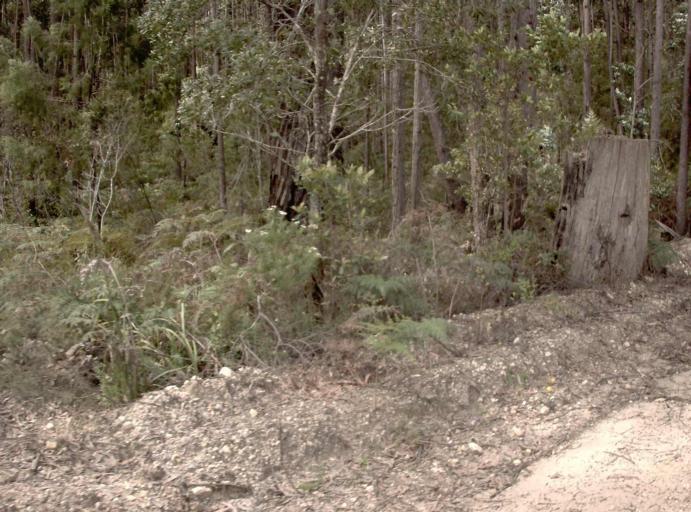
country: AU
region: Victoria
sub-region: East Gippsland
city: Lakes Entrance
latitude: -37.6225
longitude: 148.6797
